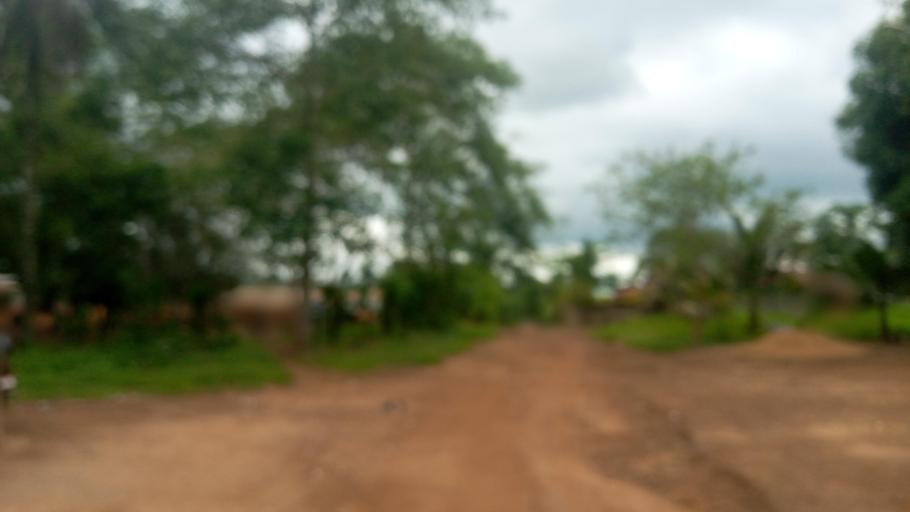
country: SL
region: Southern Province
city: Mogbwemo
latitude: 7.6006
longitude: -12.1754
